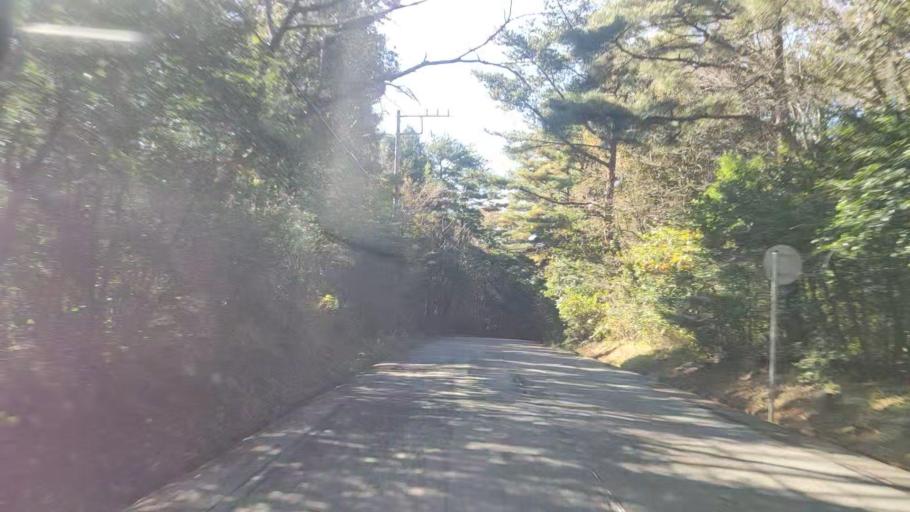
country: JP
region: Shizuoka
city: Atami
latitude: 35.0435
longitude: 139.0232
